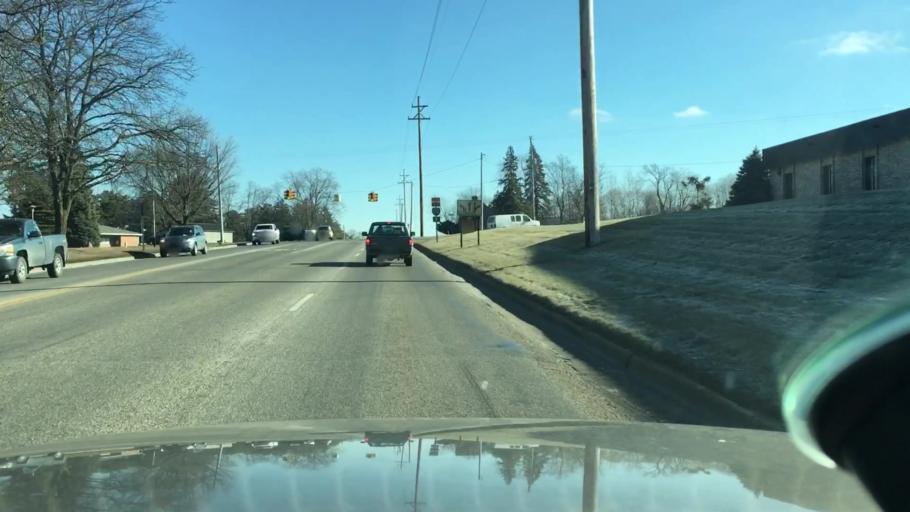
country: US
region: Michigan
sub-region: Jackson County
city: Jackson
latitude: 42.2911
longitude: -84.3985
